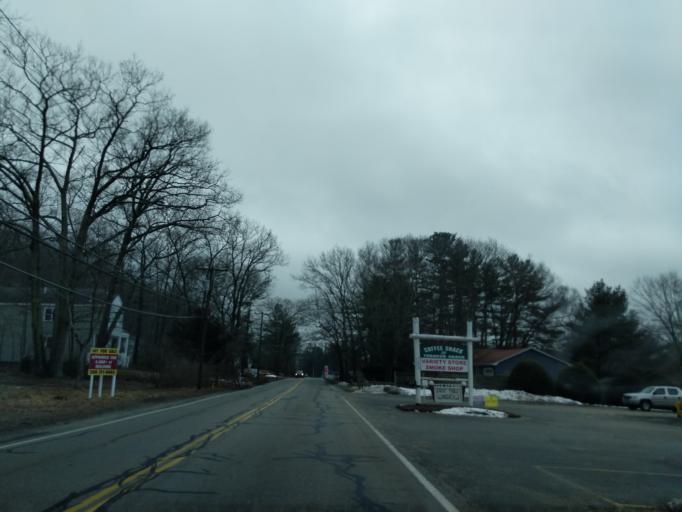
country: US
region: Massachusetts
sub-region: Worcester County
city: Webster
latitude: 42.0566
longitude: -71.8424
